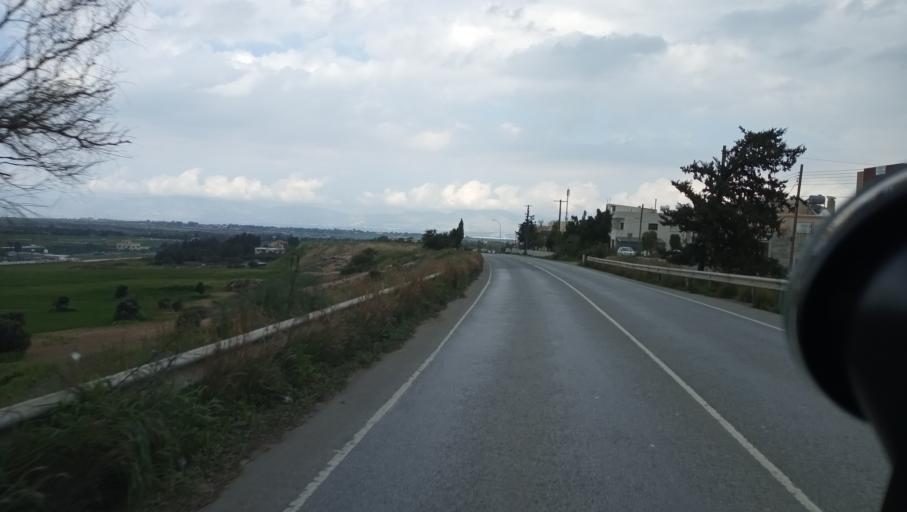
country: CY
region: Lefkosia
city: Kato Deftera
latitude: 35.1212
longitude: 33.2898
